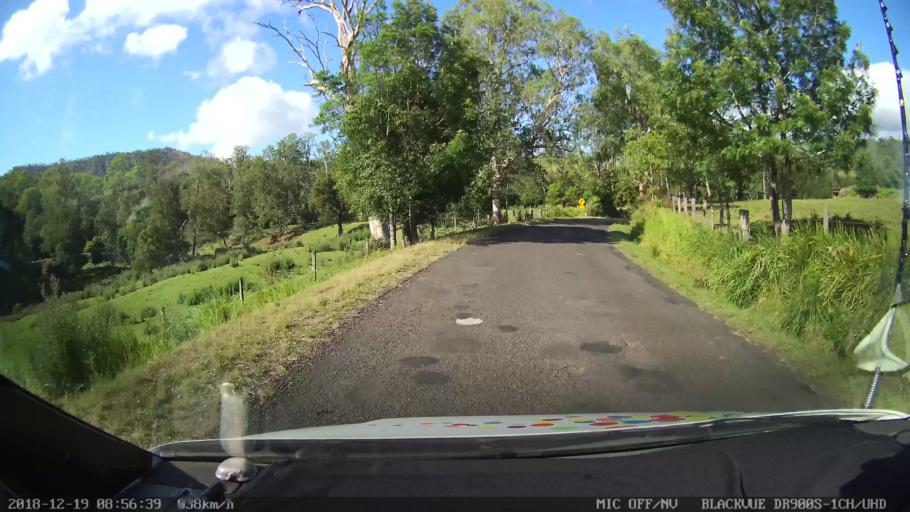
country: AU
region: New South Wales
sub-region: Kyogle
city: Kyogle
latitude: -28.4202
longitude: 152.9761
